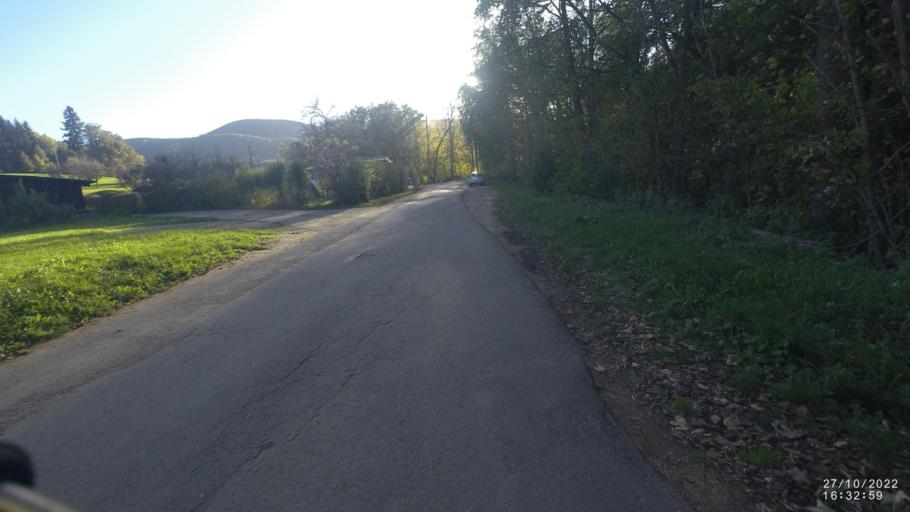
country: DE
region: Baden-Wuerttemberg
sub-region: Regierungsbezirk Stuttgart
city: Gingen an der Fils
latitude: 48.6520
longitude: 9.7765
